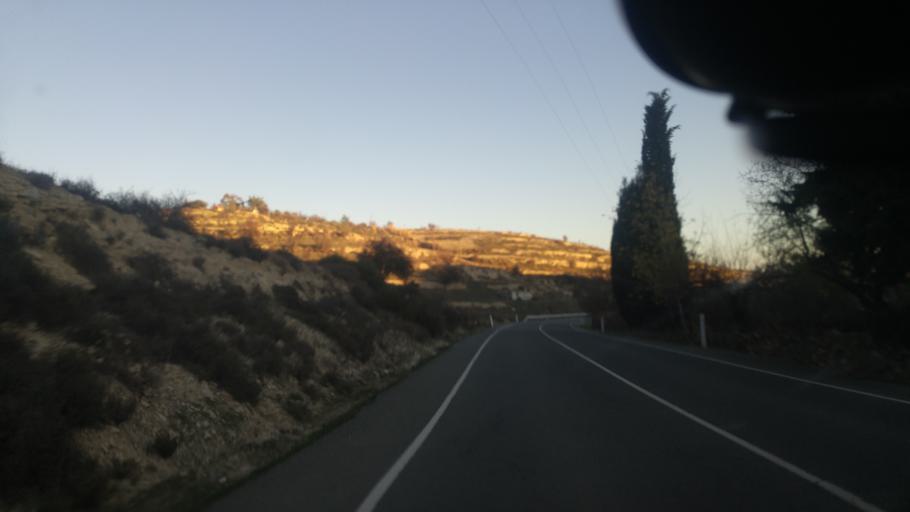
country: CY
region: Limassol
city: Pachna
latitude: 34.7945
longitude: 32.8194
